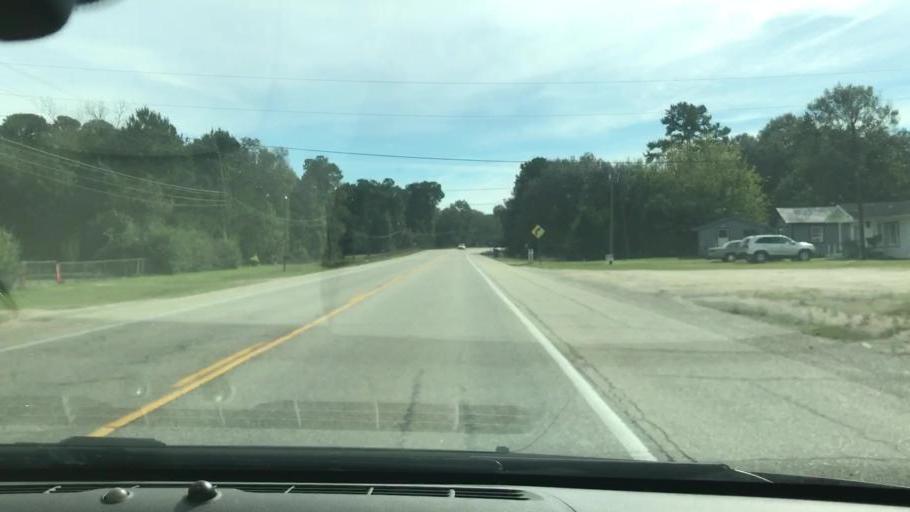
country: US
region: Louisiana
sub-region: Saint Tammany Parish
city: Pearl River
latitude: 30.4409
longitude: -89.7903
